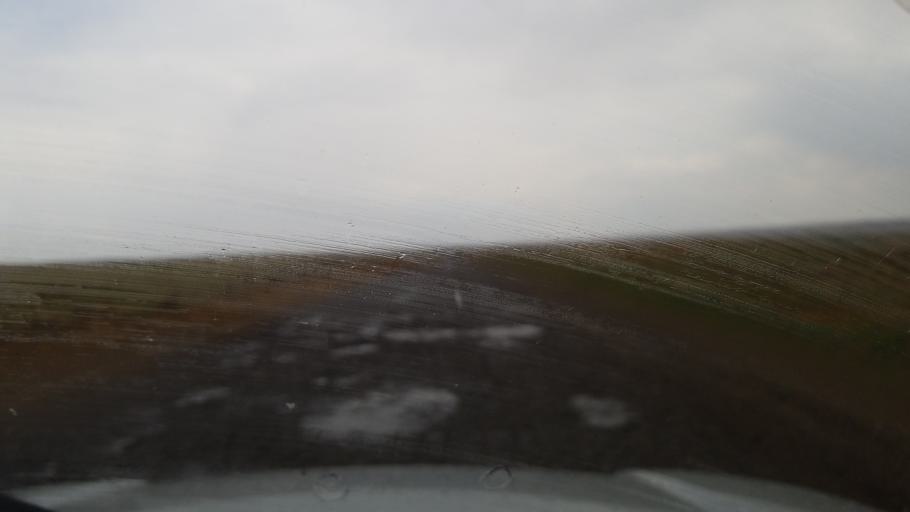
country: TM
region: Mary
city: Serhetabat
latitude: 35.8806
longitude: 62.6207
